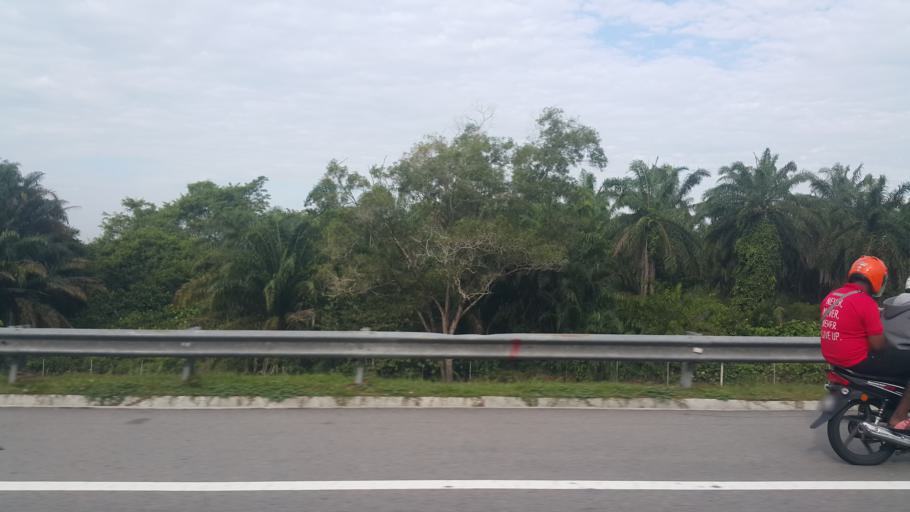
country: MY
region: Johor
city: Pekan Nenas
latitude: 1.3853
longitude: 103.5926
